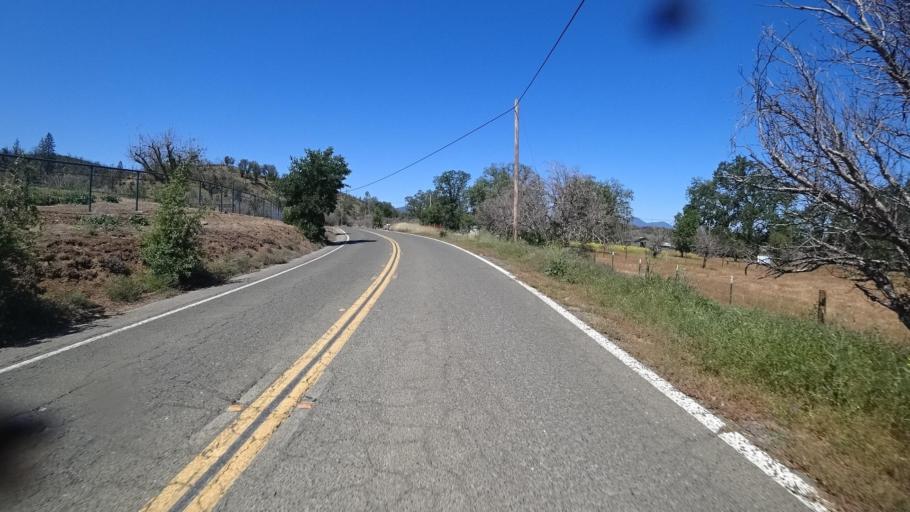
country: US
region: California
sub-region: Lake County
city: Lower Lake
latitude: 38.9087
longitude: -122.5843
